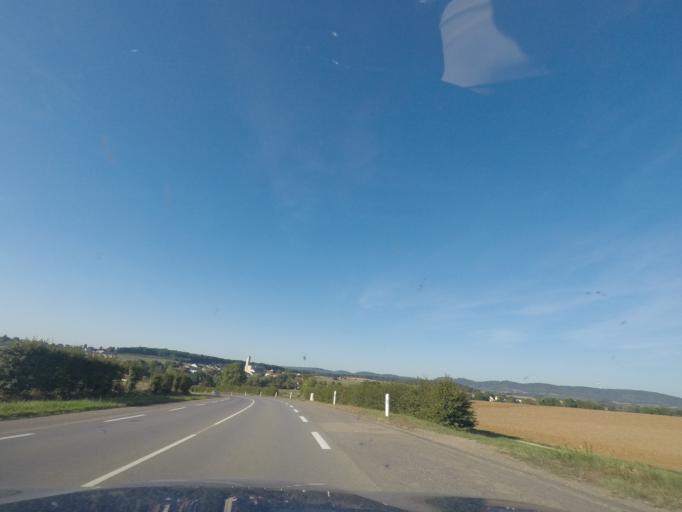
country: LU
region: Luxembourg
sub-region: Canton d'Esch-sur-Alzette
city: Frisange
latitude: 49.4616
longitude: 6.1792
